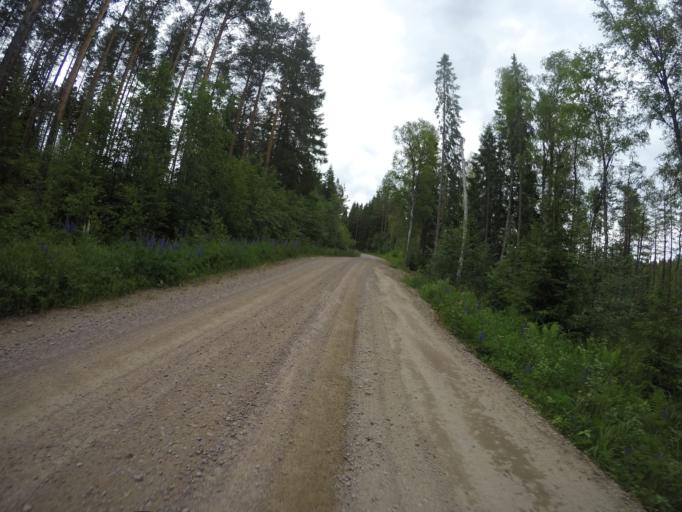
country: SE
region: Dalarna
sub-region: Ludvika Kommun
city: Abborrberget
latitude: 60.0969
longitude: 14.5405
